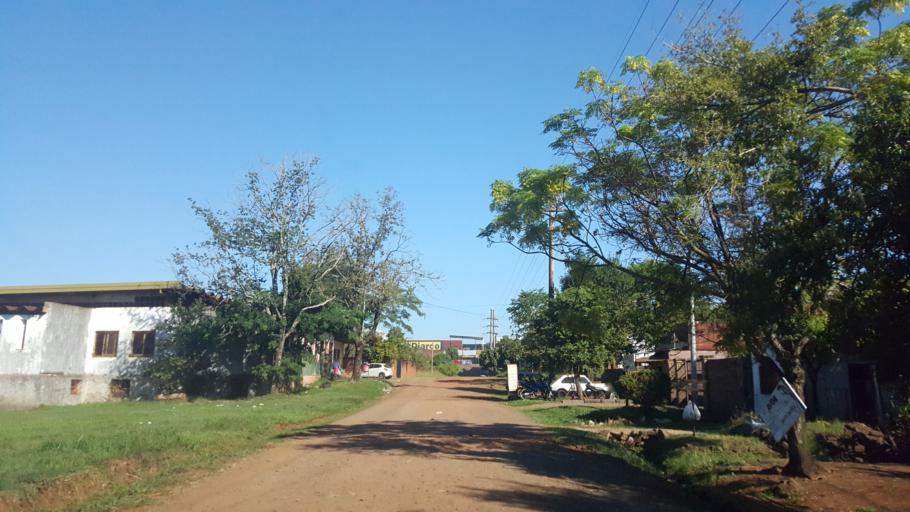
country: AR
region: Misiones
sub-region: Departamento de Capital
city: Posadas
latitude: -27.4059
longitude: -55.9000
